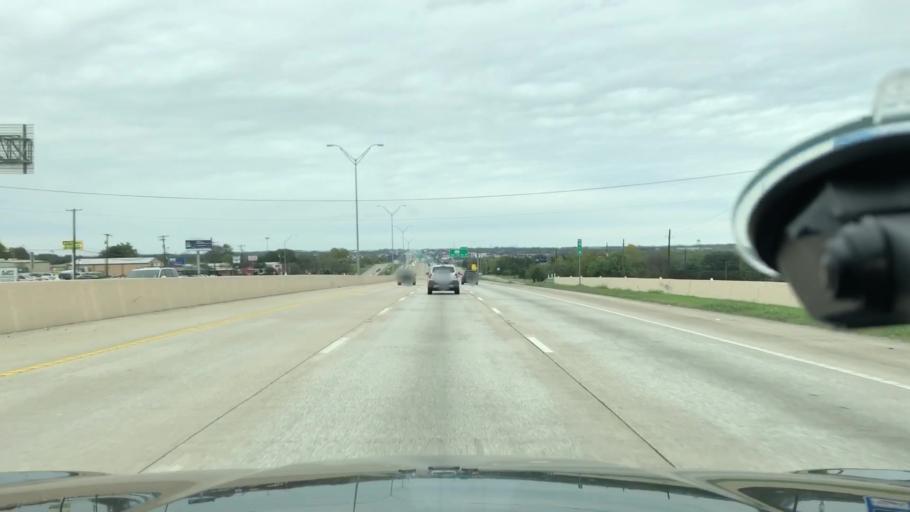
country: US
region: Texas
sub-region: Dallas County
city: DeSoto
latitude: 32.5761
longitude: -96.8223
